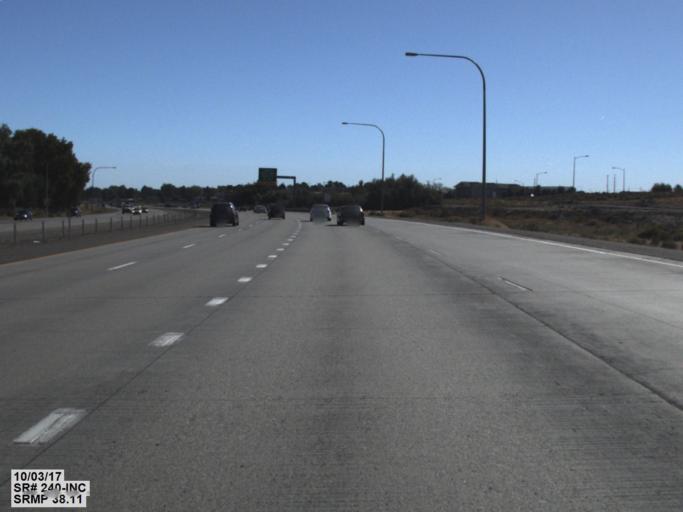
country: US
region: Washington
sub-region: Franklin County
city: West Pasco
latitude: 46.2352
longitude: -119.2386
